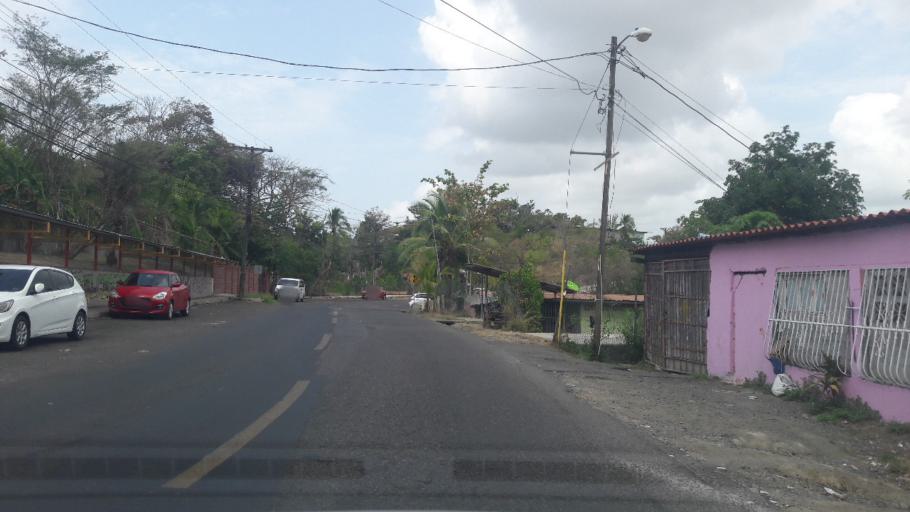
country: PA
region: Panama
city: Alcalde Diaz
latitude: 9.1131
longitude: -79.5556
